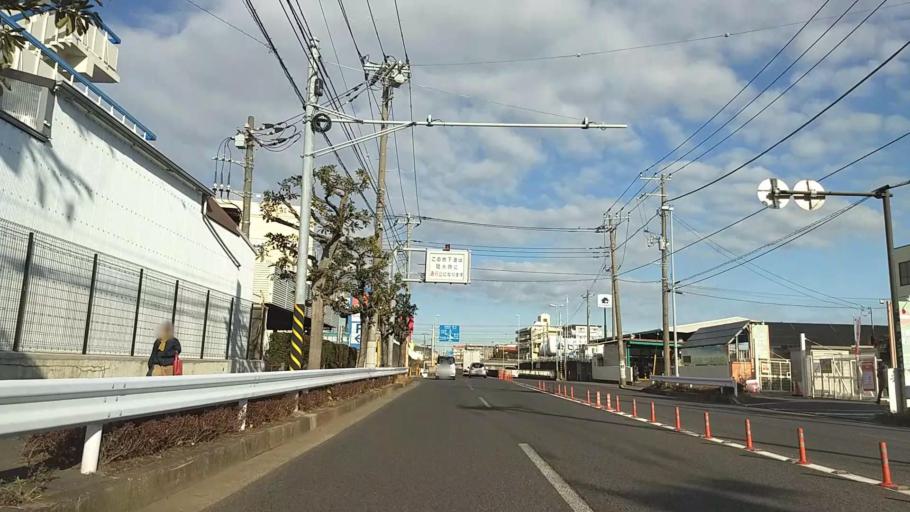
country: JP
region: Kanagawa
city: Hiratsuka
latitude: 35.3278
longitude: 139.3599
